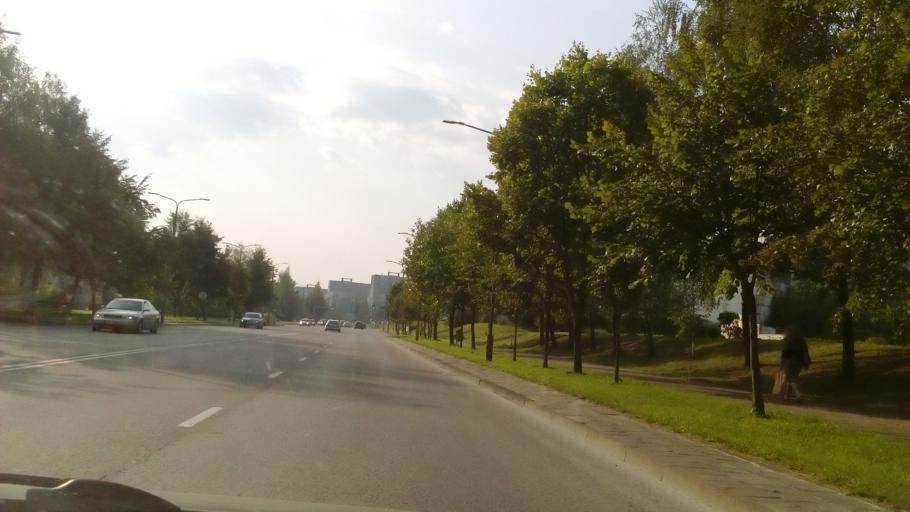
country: LT
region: Alytaus apskritis
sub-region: Alytus
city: Alytus
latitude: 54.3962
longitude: 24.0166
